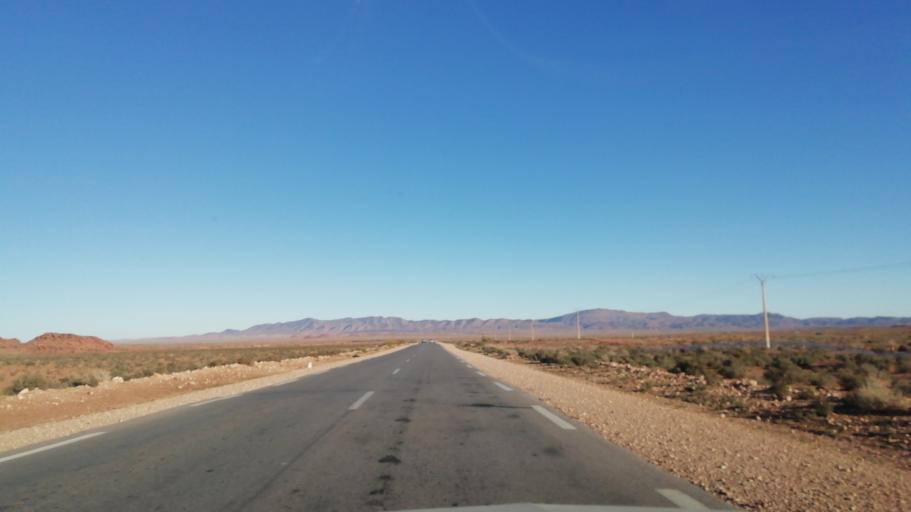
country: DZ
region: El Bayadh
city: El Abiodh Sidi Cheikh
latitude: 33.1699
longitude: 0.5024
